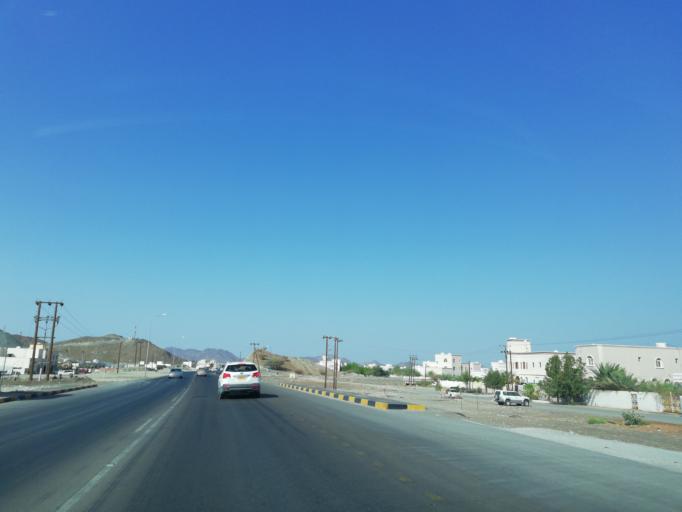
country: OM
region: Ash Sharqiyah
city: Ibra'
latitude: 22.7980
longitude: 58.1559
